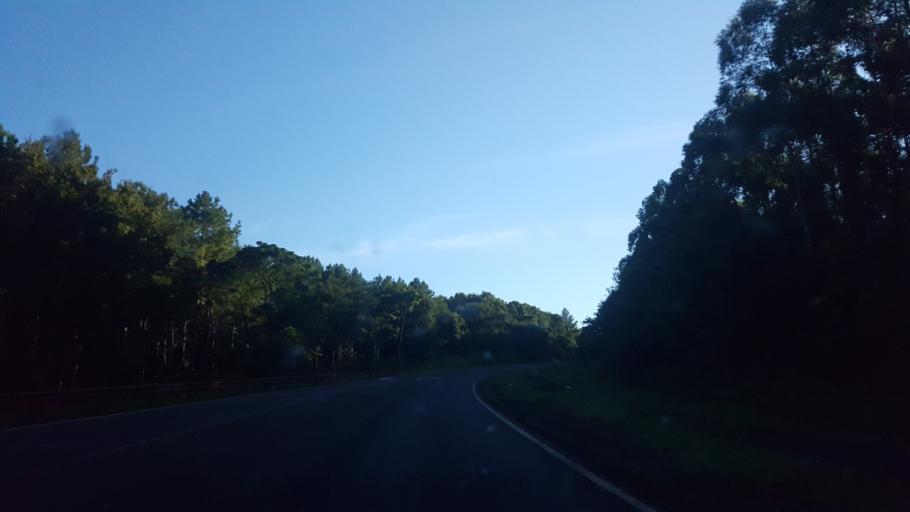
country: AR
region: Misiones
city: Caraguatay
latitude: -26.6633
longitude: -54.7544
